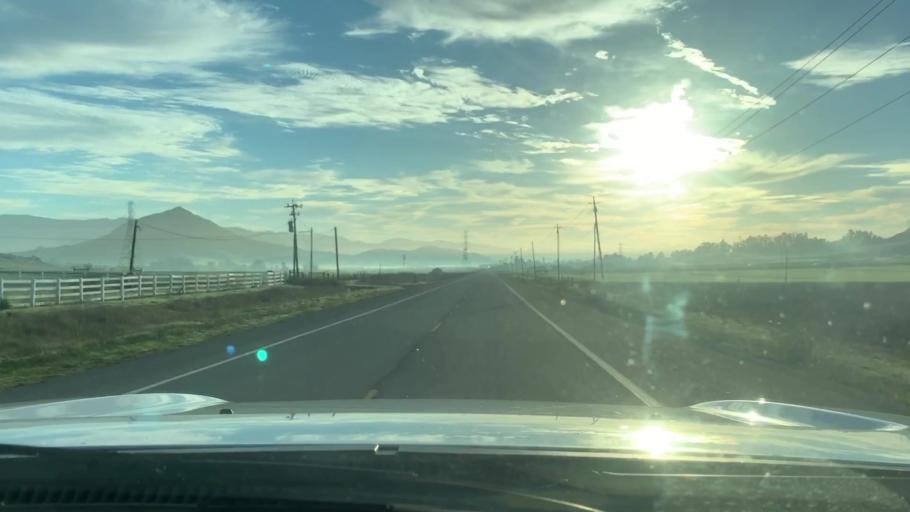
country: US
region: California
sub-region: San Luis Obispo County
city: San Luis Obispo
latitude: 35.2849
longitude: -120.7340
